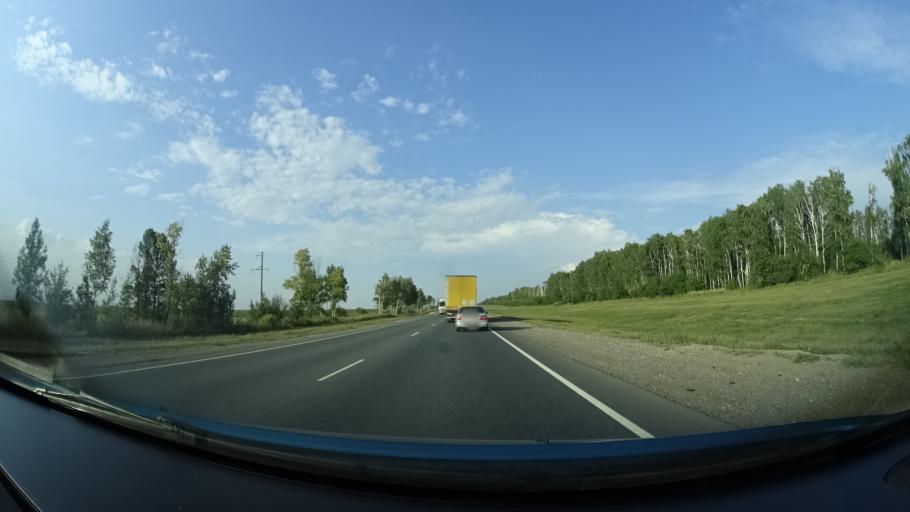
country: RU
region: Samara
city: Krasnyy Yar
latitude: 53.6581
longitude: 50.7511
